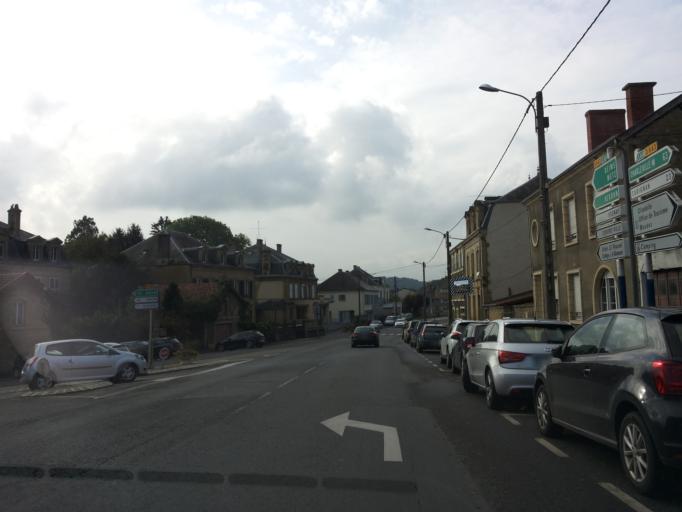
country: FR
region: Lorraine
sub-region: Departement de la Meuse
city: Montmedy
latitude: 49.5226
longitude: 5.3691
